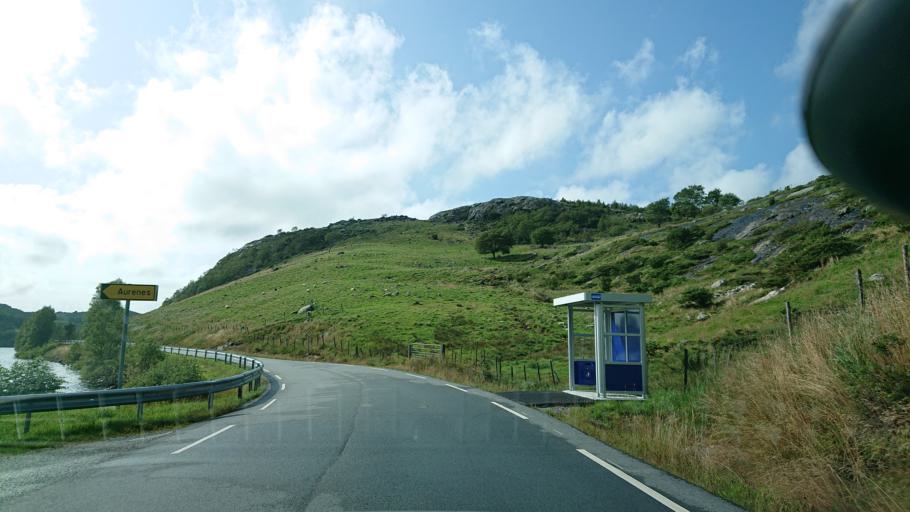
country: NO
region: Rogaland
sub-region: Gjesdal
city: Algard
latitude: 58.6774
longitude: 5.8377
